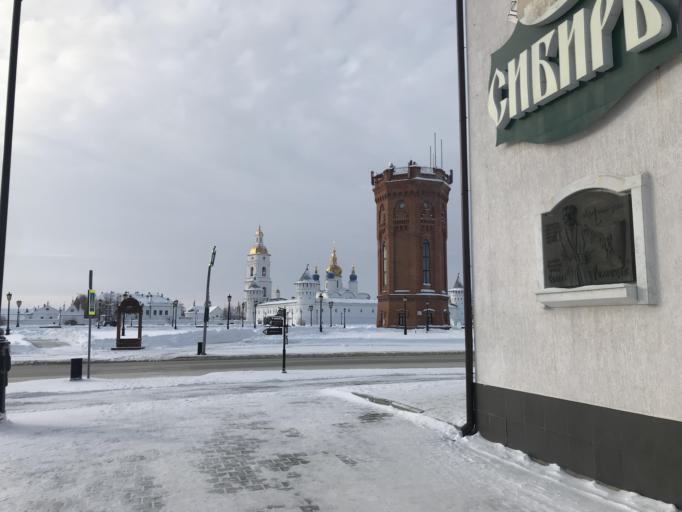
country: RU
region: Tjumen
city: Tobol'sk
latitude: 58.2008
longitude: 68.2558
